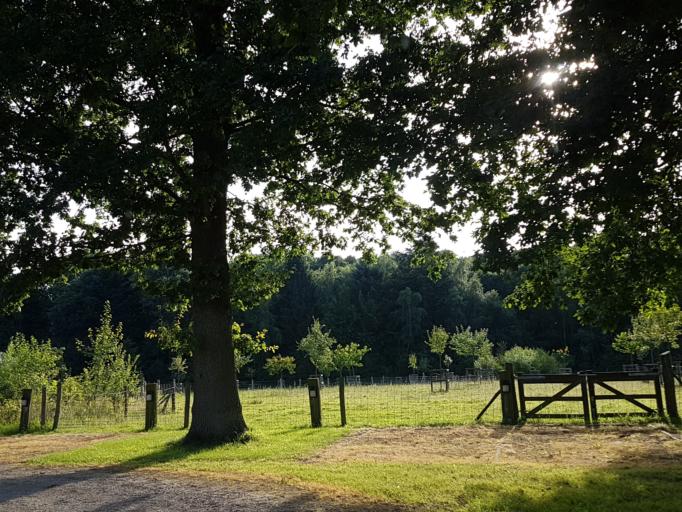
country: BE
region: Flanders
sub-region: Provincie Oost-Vlaanderen
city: Denderleeuw
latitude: 50.9318
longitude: 4.0972
